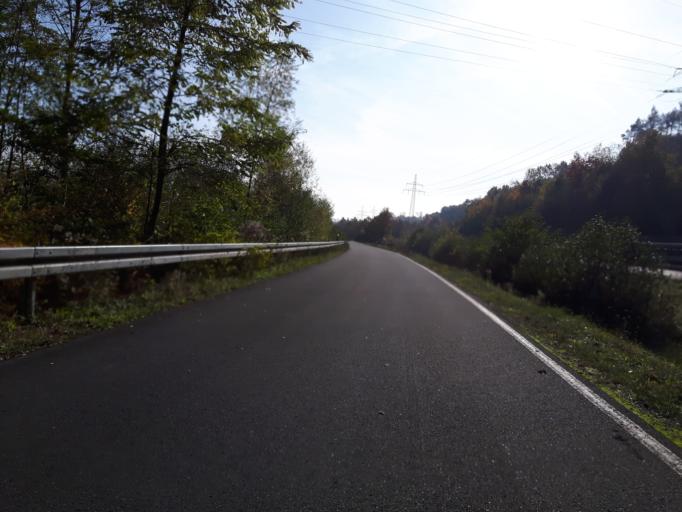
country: DE
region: Bavaria
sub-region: Regierungsbezirk Unterfranken
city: Worth am Main
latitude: 49.8077
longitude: 9.1355
